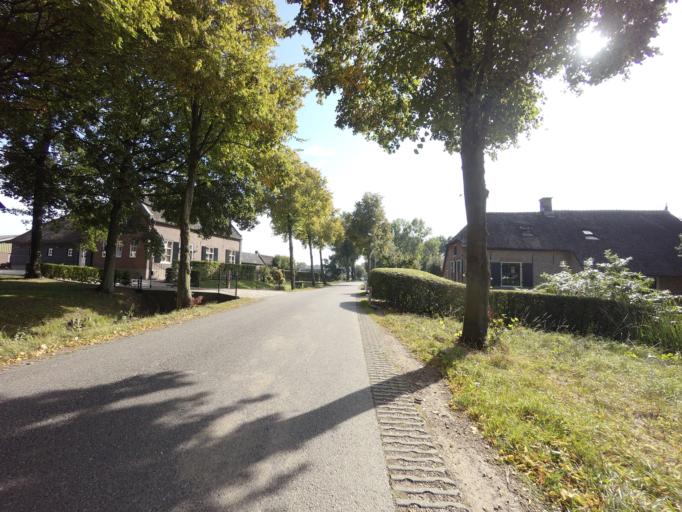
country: NL
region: South Holland
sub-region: Gemeente Leerdam
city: Leerdam
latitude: 51.9183
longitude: 5.0683
